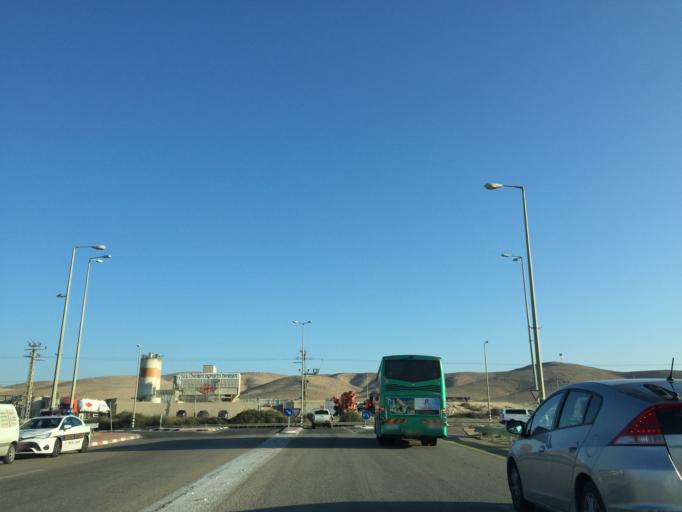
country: IL
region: Southern District
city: Dimona
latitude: 31.0676
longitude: 35.0062
